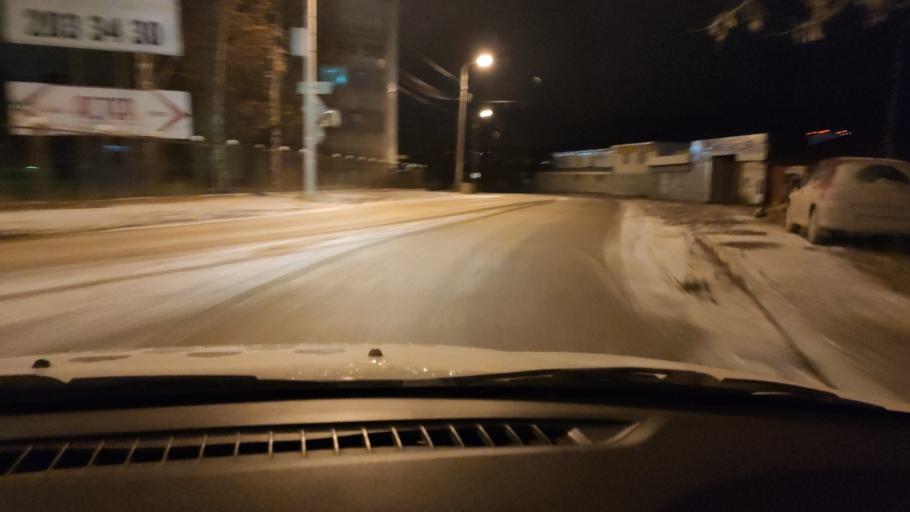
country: RU
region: Perm
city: Perm
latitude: 57.9771
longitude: 56.2672
